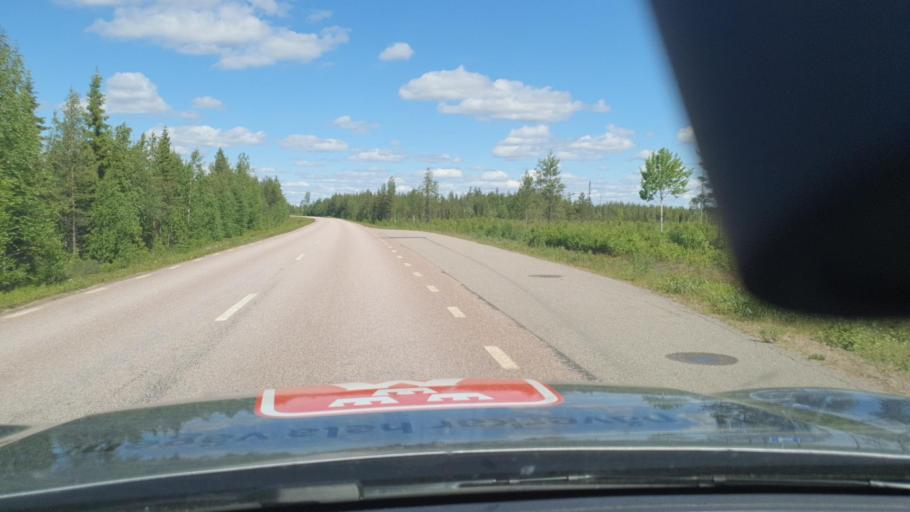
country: SE
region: Norrbotten
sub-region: Pajala Kommun
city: Pajala
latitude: 67.2221
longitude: 22.7870
